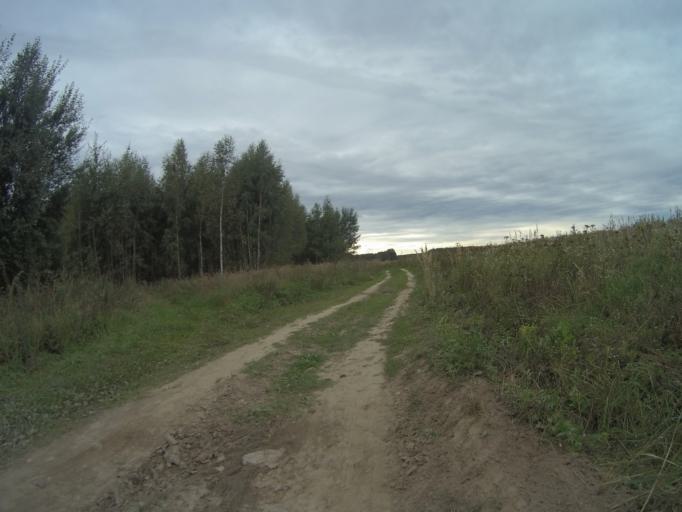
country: RU
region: Vladimir
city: Golovino
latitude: 55.9769
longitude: 40.4836
